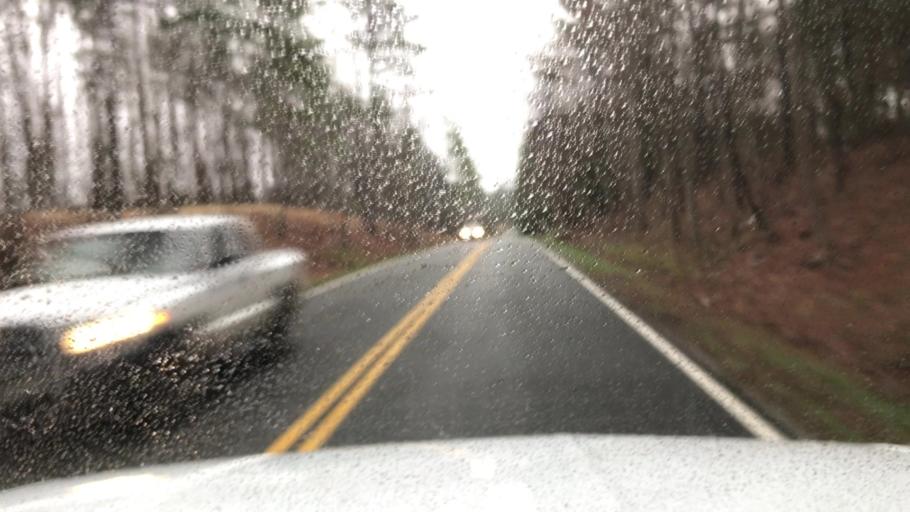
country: US
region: Virginia
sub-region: Henrico County
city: Short Pump
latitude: 37.6561
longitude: -77.6783
